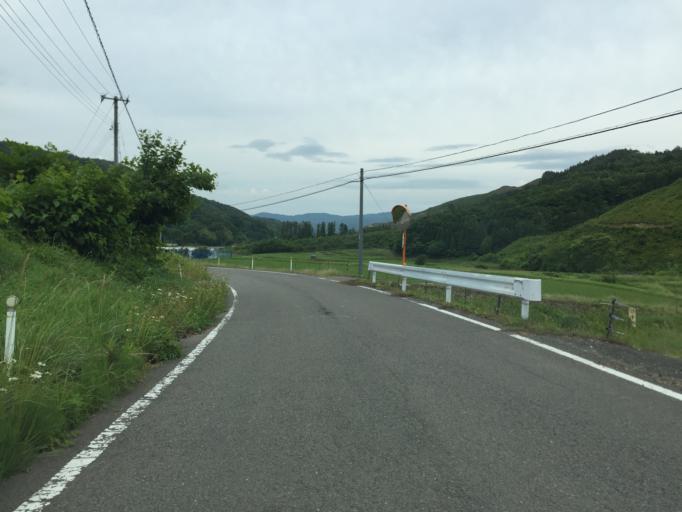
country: JP
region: Fukushima
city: Funehikimachi-funehiki
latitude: 37.4289
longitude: 140.7475
